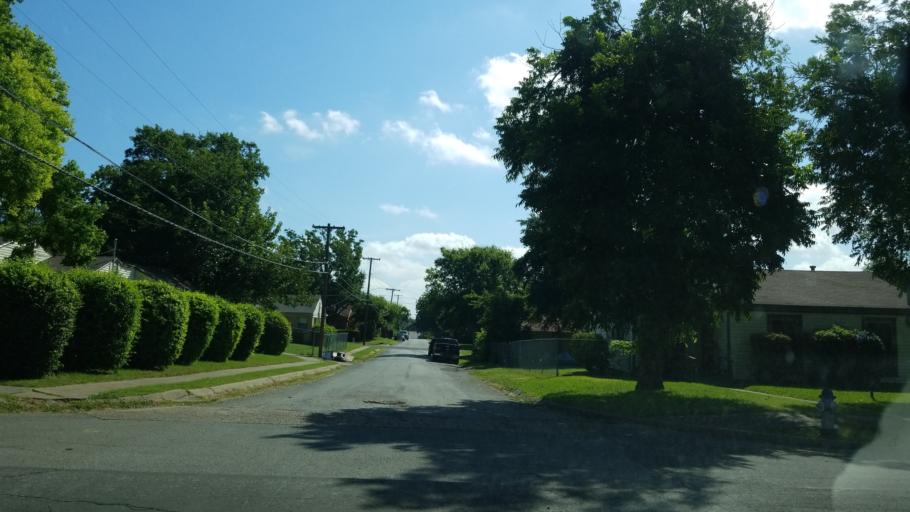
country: US
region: Texas
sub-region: Dallas County
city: Dallas
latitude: 32.7153
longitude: -96.7969
